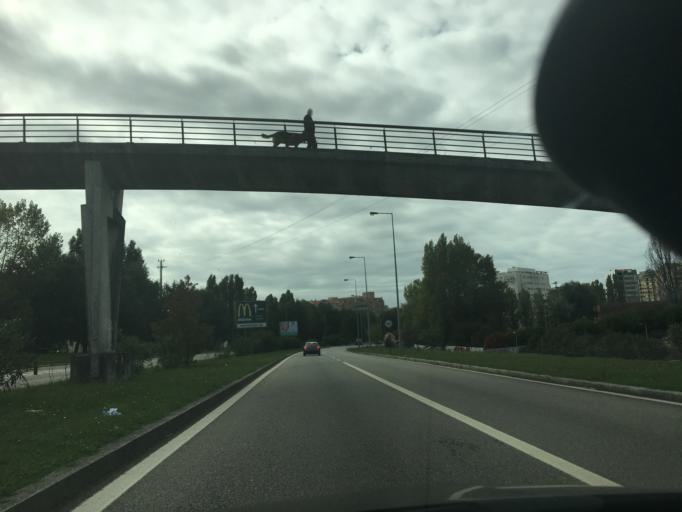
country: PT
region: Porto
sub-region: Matosinhos
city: Matosinhos
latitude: 41.1825
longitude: -8.6773
